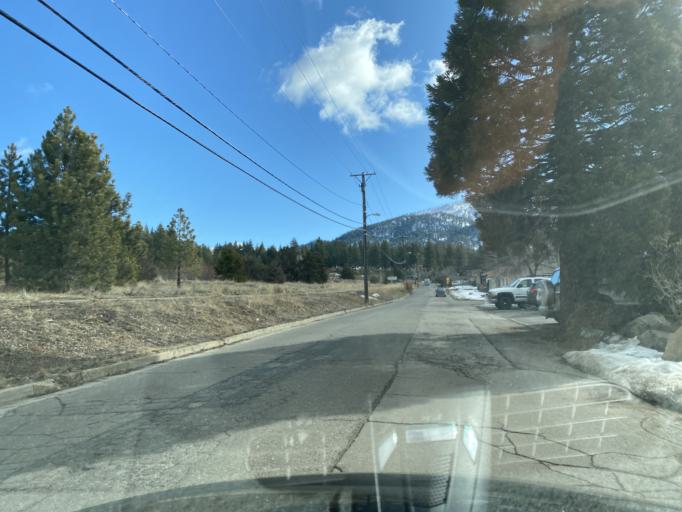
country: US
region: Nevada
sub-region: Douglas County
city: Kingsbury
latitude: 38.9718
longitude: -119.9389
